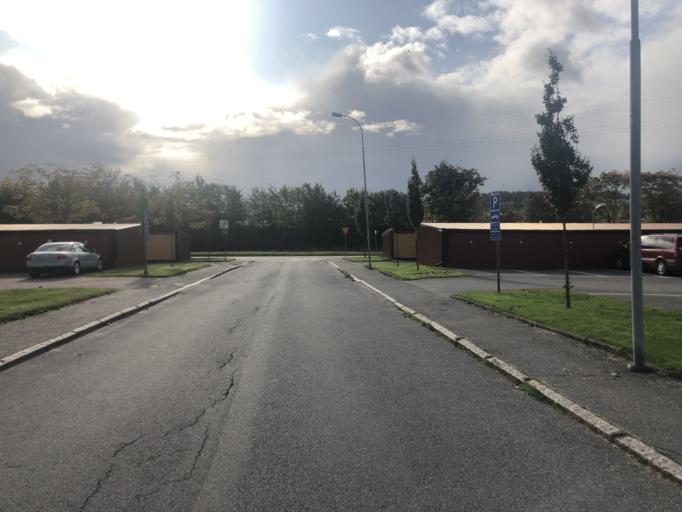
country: SE
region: Vaestra Goetaland
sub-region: Molndal
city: Moelndal
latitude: 57.6454
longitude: 12.0100
